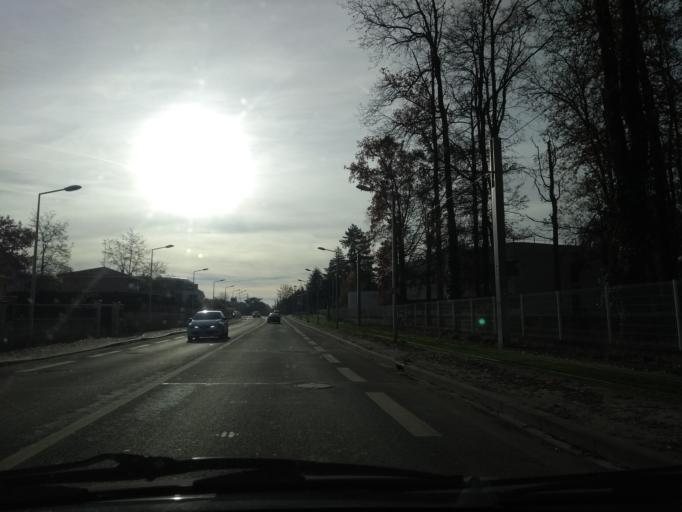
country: FR
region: Aquitaine
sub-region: Departement de la Gironde
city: Pessac
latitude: 44.7893
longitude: -0.6563
